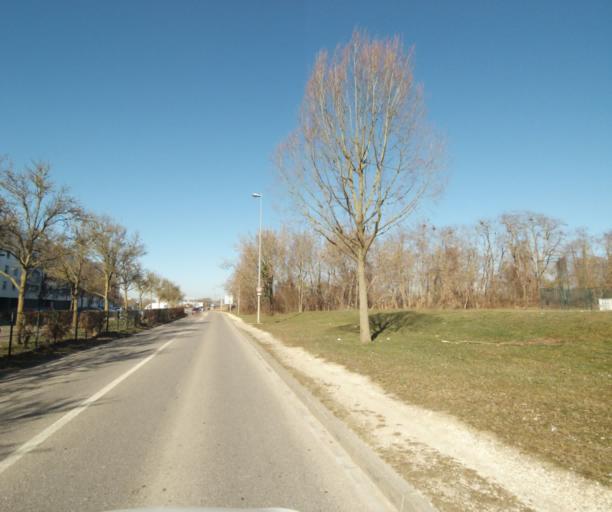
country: FR
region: Lorraine
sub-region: Departement de Meurthe-et-Moselle
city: Jarville-la-Malgrange
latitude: 48.6730
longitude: 6.2091
